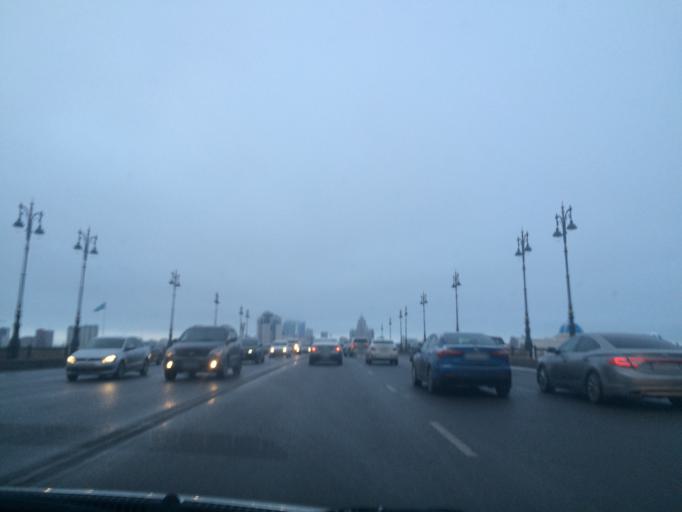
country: KZ
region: Astana Qalasy
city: Astana
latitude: 51.1586
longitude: 71.4110
